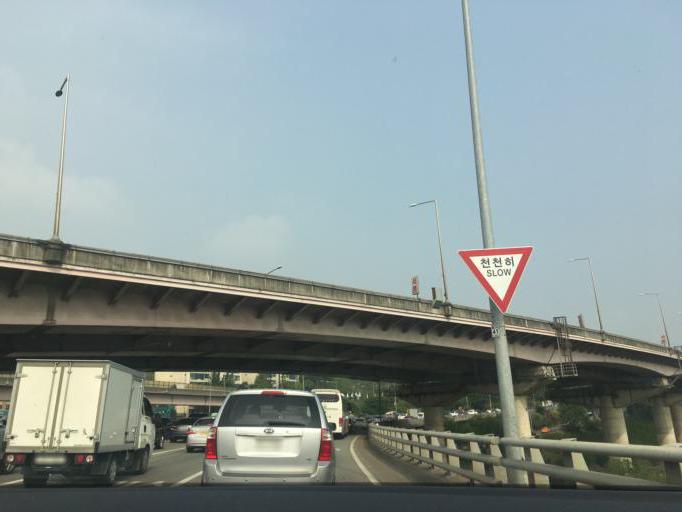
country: KR
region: Seoul
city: Seoul
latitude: 37.5186
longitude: 127.0667
